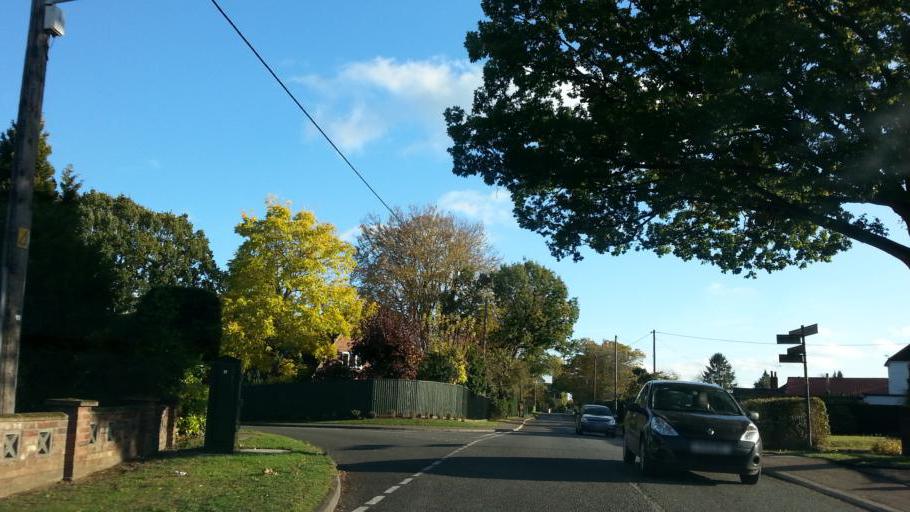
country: GB
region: England
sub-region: Suffolk
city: Great Barton
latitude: 52.2722
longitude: 0.7882
